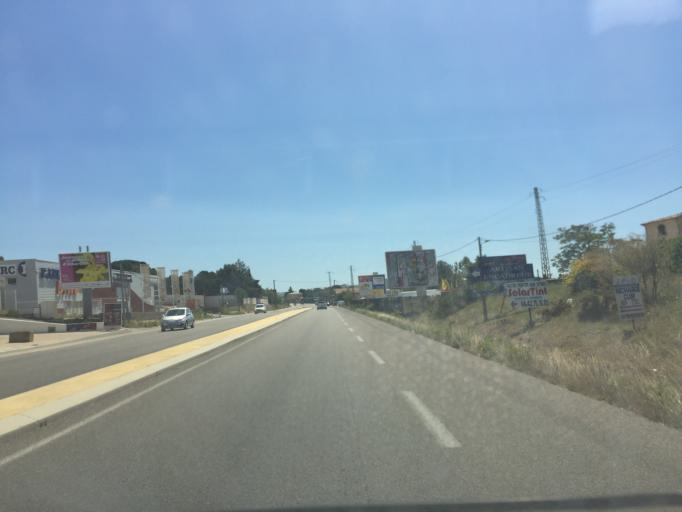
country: FR
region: Provence-Alpes-Cote d'Azur
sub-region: Departement des Bouches-du-Rhone
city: Vitrolles
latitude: 43.4662
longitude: 5.2319
